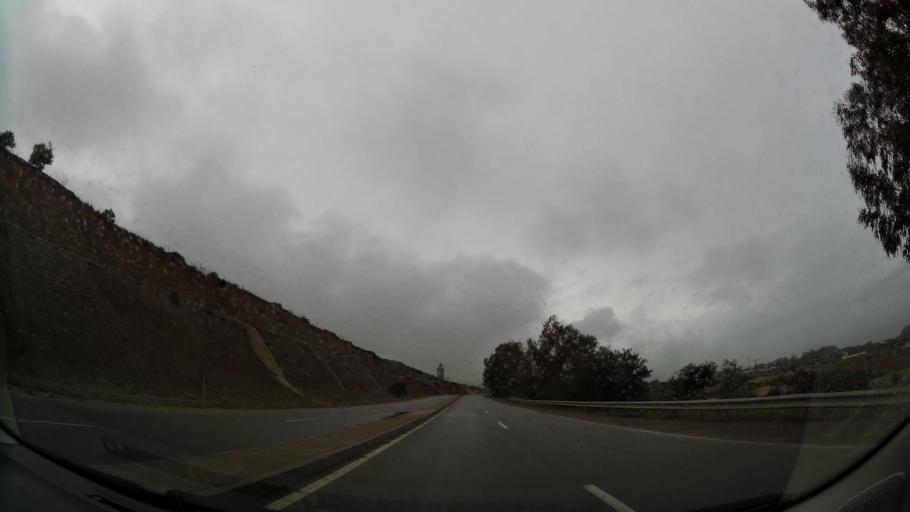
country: MA
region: Taza-Al Hoceima-Taounate
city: Imzourene
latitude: 35.1886
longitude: -3.8848
